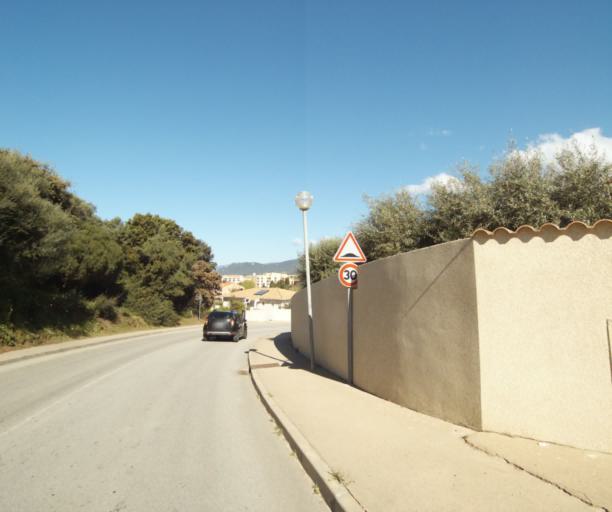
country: FR
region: Corsica
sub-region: Departement de la Corse-du-Sud
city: Propriano
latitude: 41.6717
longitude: 8.9059
